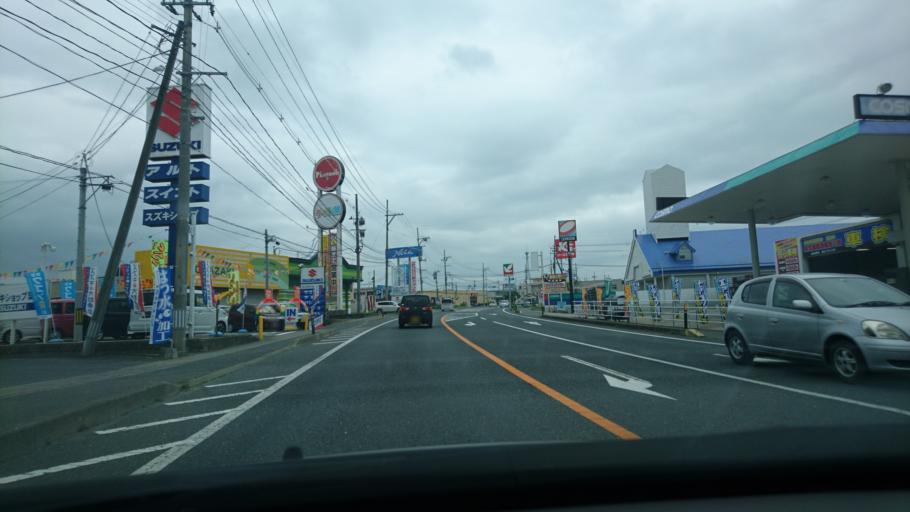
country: JP
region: Miyagi
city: Furukawa
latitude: 38.7378
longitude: 141.0216
